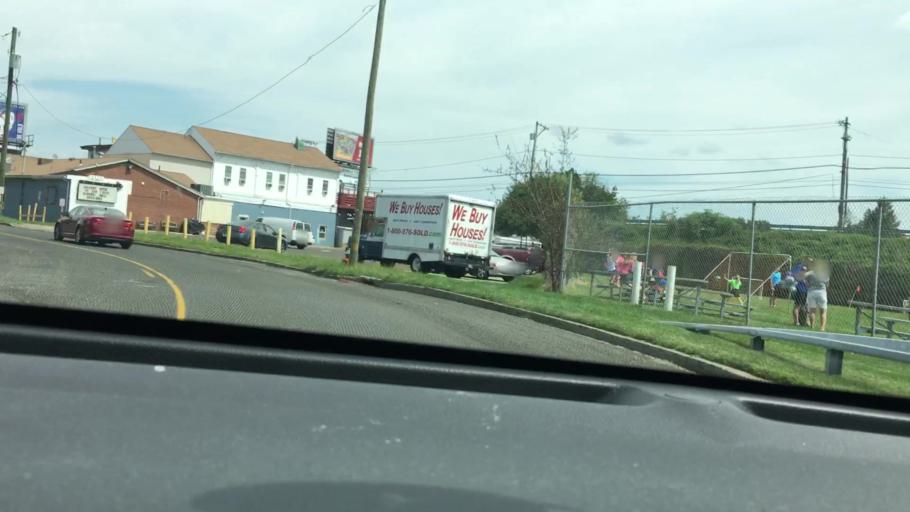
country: US
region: Pennsylvania
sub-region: Bucks County
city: Feasterville
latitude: 40.1309
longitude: -75.0141
